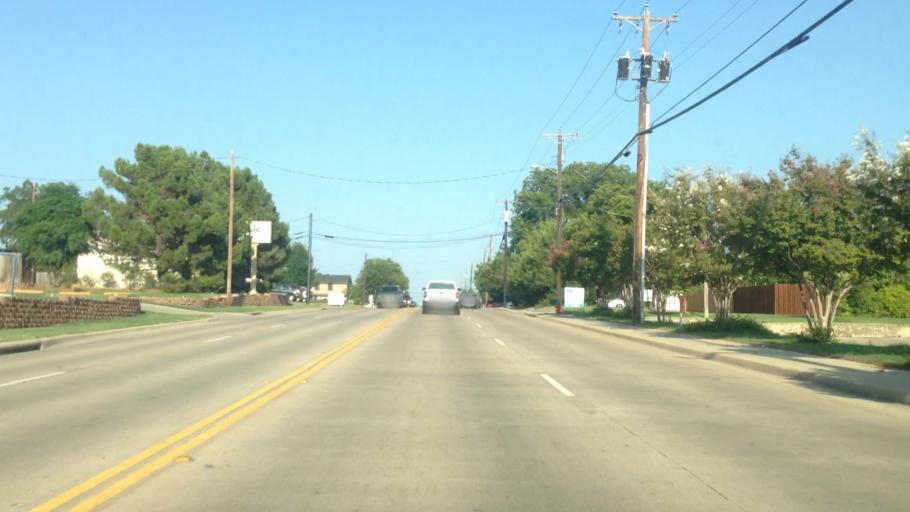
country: US
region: Texas
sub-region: Tarrant County
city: Haltom City
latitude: 32.8097
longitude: -97.2867
